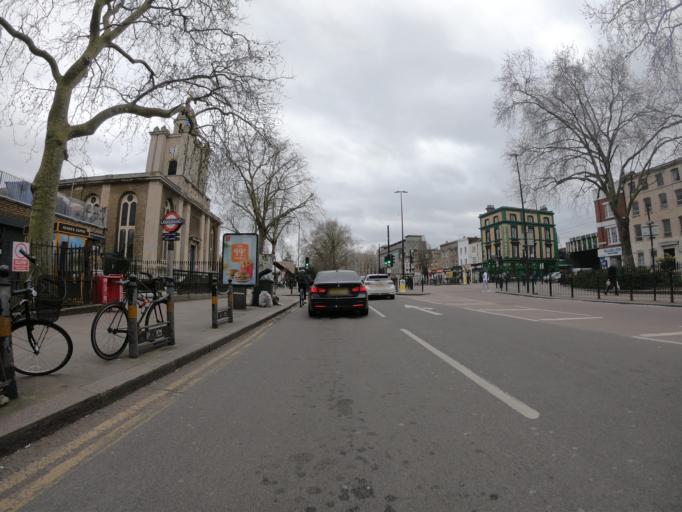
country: GB
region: England
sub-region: Greater London
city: Bethnal Green
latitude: 51.5279
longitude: -0.0554
